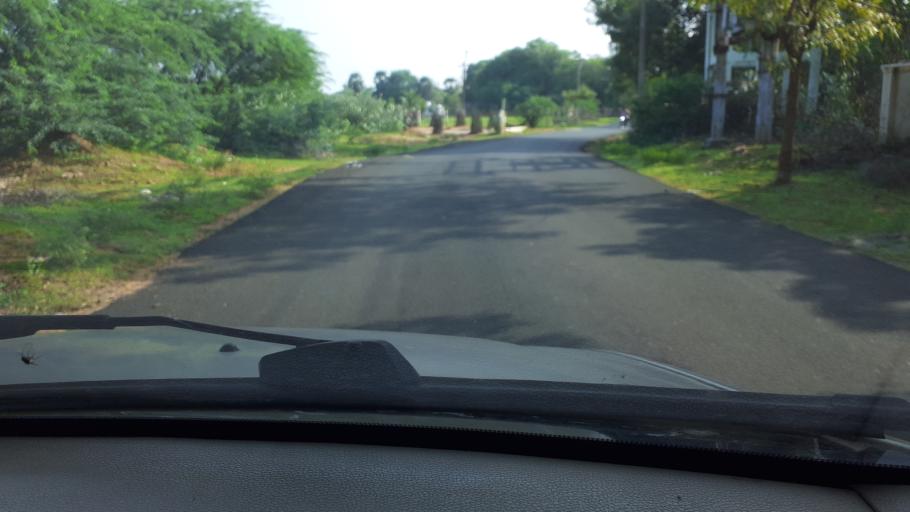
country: IN
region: Tamil Nadu
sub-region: Thoothukkudi
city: Eral
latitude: 8.5764
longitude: 78.0224
